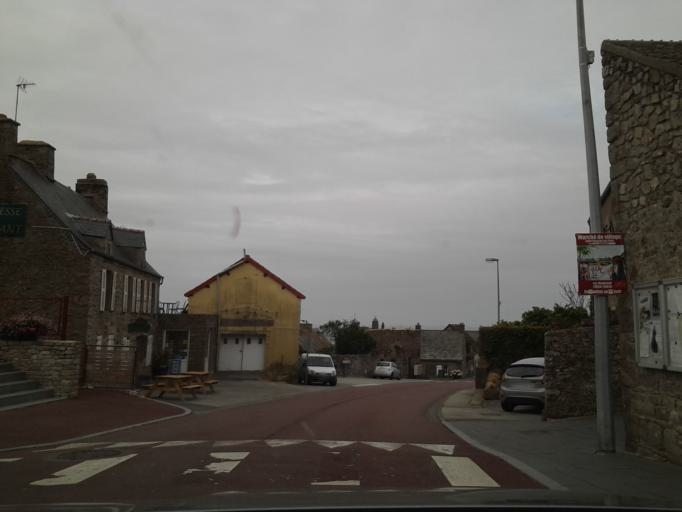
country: FR
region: Lower Normandy
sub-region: Departement de la Manche
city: Beaumont-Hague
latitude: 49.7114
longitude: -1.9320
